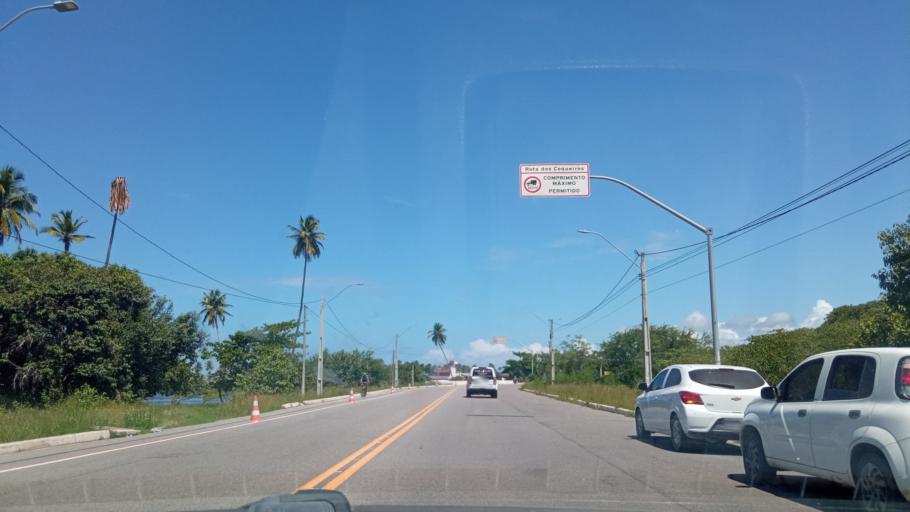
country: BR
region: Pernambuco
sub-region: Jaboatao Dos Guararapes
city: Jaboatao
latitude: -8.2361
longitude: -34.9370
